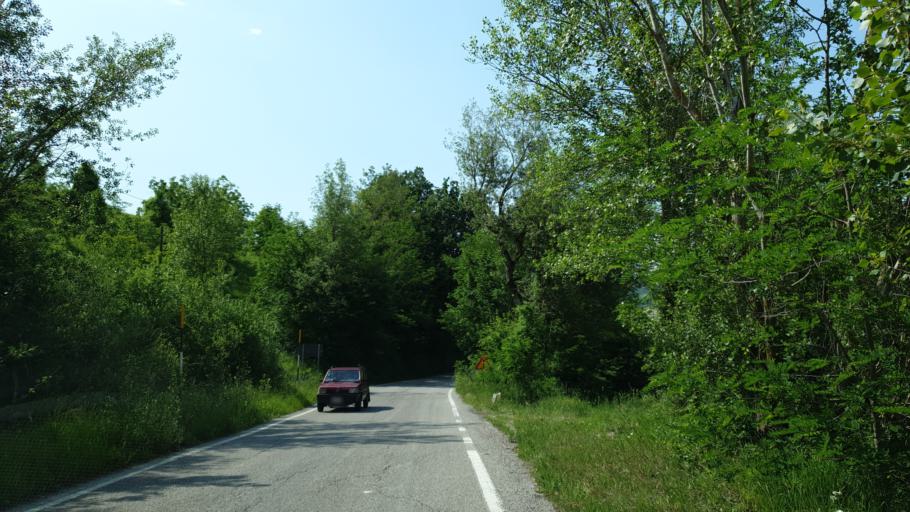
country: IT
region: Emilia-Romagna
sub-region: Forli-Cesena
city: Sarsina
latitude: 43.9109
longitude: 12.1763
